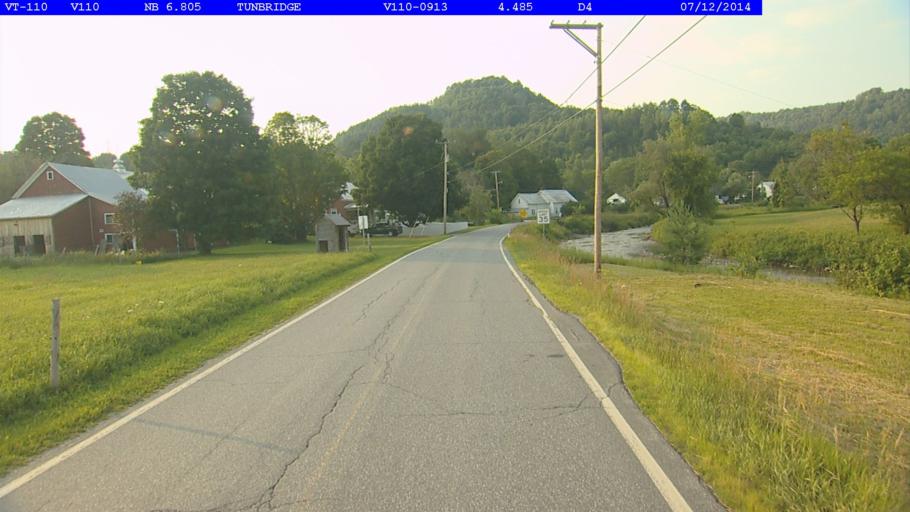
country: US
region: Vermont
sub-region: Orange County
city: Chelsea
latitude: 43.9094
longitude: -72.4831
